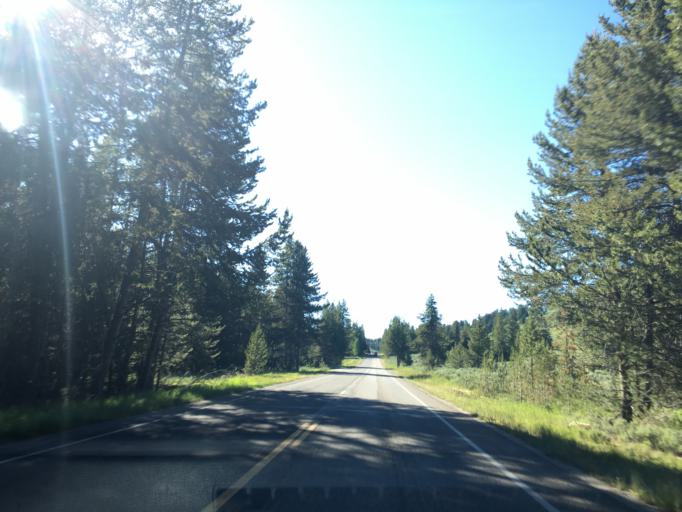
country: US
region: Wyoming
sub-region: Teton County
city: Jackson
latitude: 43.8589
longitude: -110.5293
